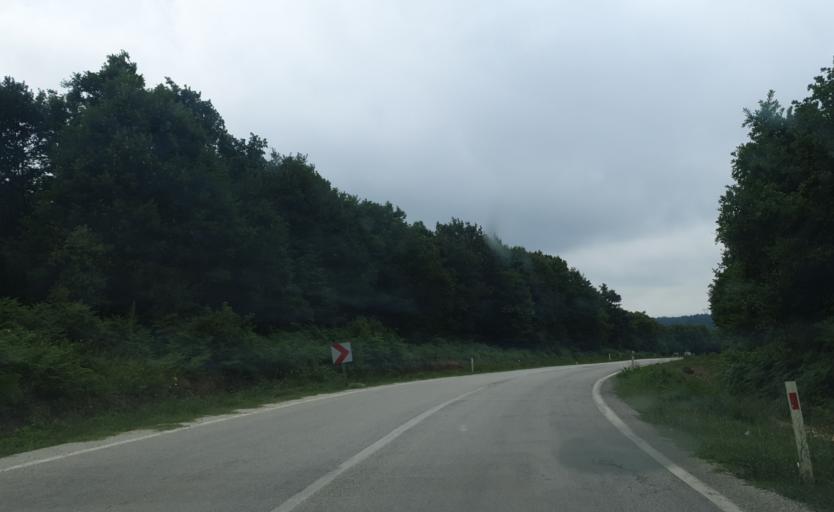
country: TR
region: Kirklareli
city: Salmydessus
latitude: 41.5789
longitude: 28.0718
